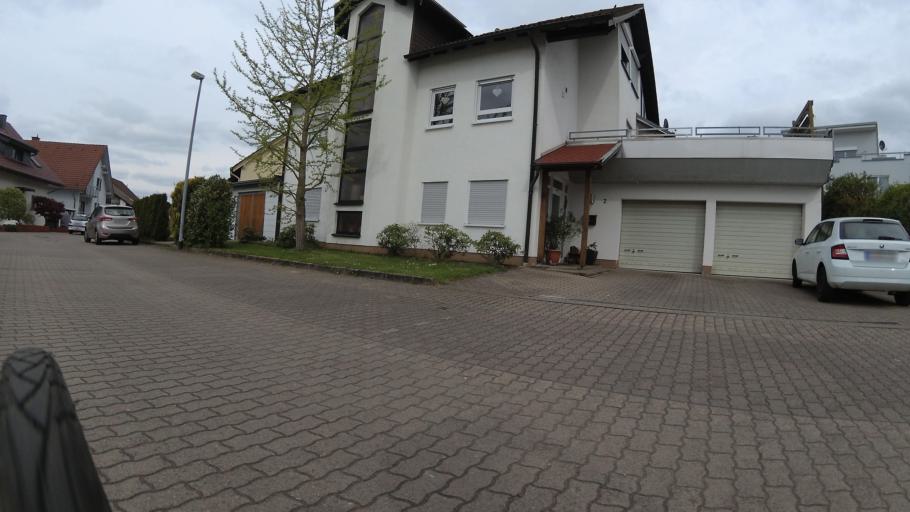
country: DE
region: Rheinland-Pfalz
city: Zweibrucken
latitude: 49.2347
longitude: 7.3741
